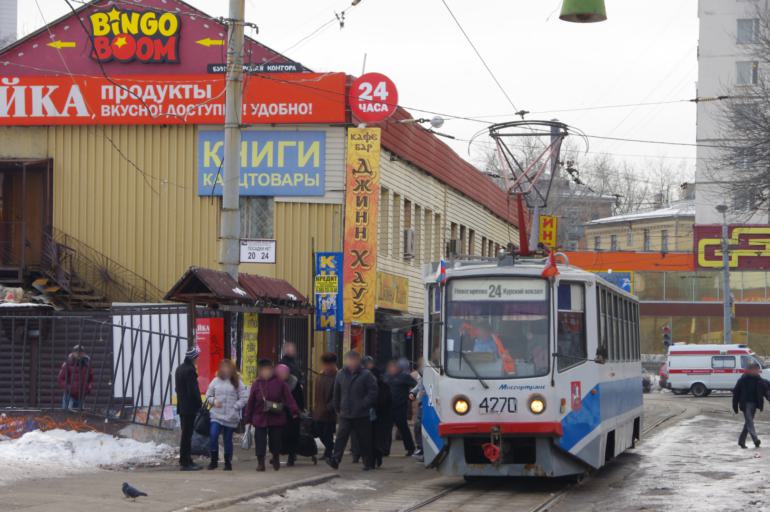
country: RU
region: Moscow
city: Taganskiy
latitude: 55.7557
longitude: 37.6607
